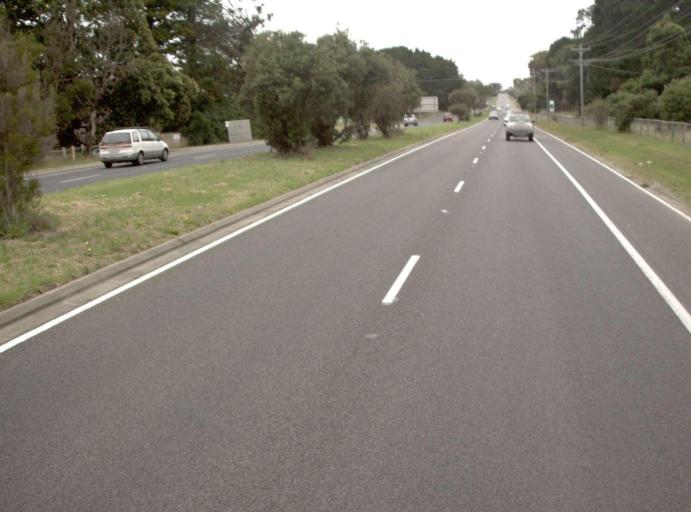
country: AU
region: Victoria
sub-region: Mornington Peninsula
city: Mount Eliza
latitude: -38.2063
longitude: 145.0749
